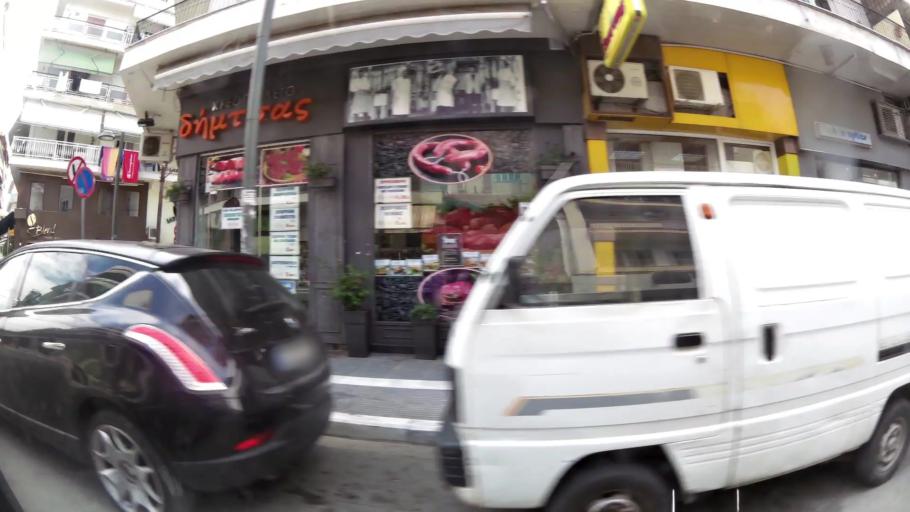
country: GR
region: Central Macedonia
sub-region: Nomos Pierias
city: Katerini
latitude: 40.2723
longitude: 22.5091
